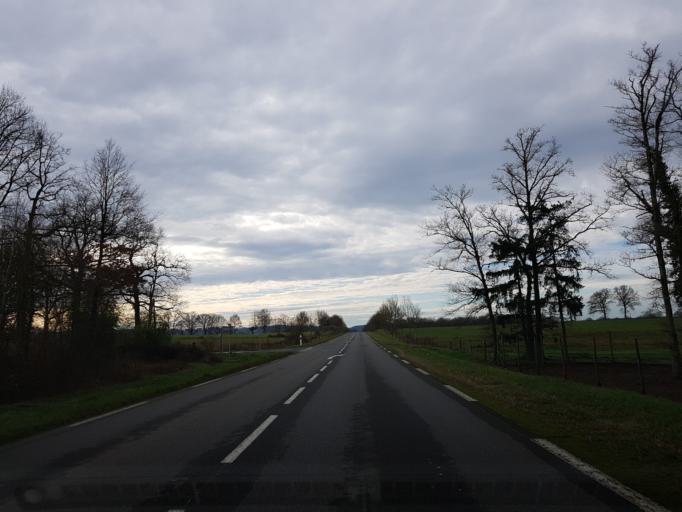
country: FR
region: Limousin
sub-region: Departement de la Haute-Vienne
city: Bellac
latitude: 46.0912
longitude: 1.0034
